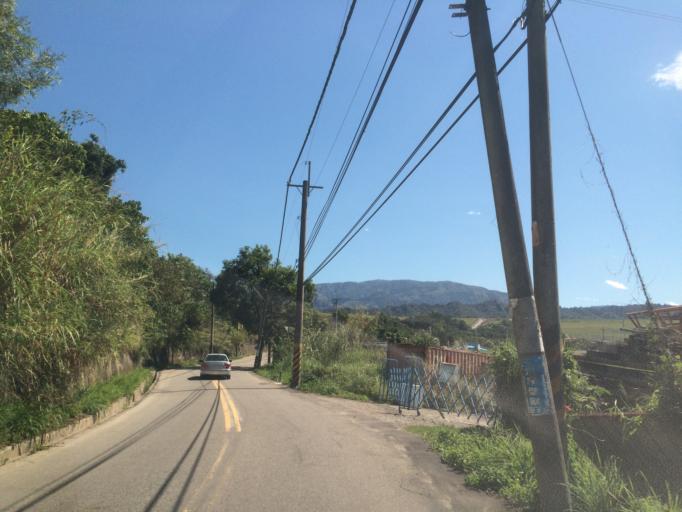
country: TW
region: Taiwan
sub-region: Yunlin
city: Douliu
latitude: 23.6997
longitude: 120.6162
